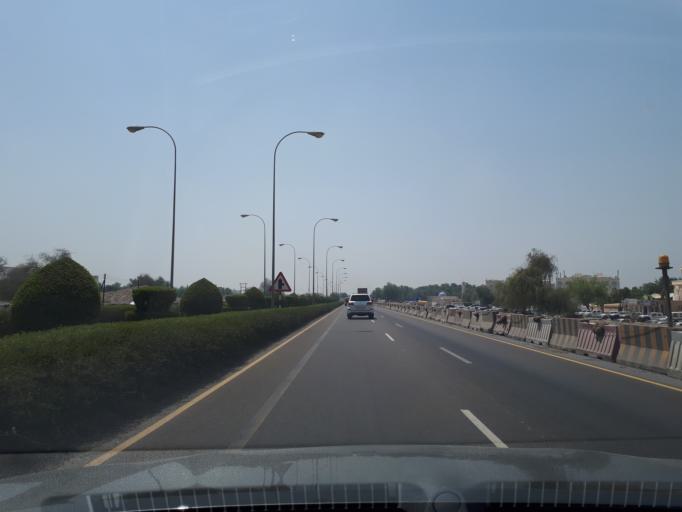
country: OM
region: Al Batinah
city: Al Sohar
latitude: 24.3908
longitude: 56.6959
